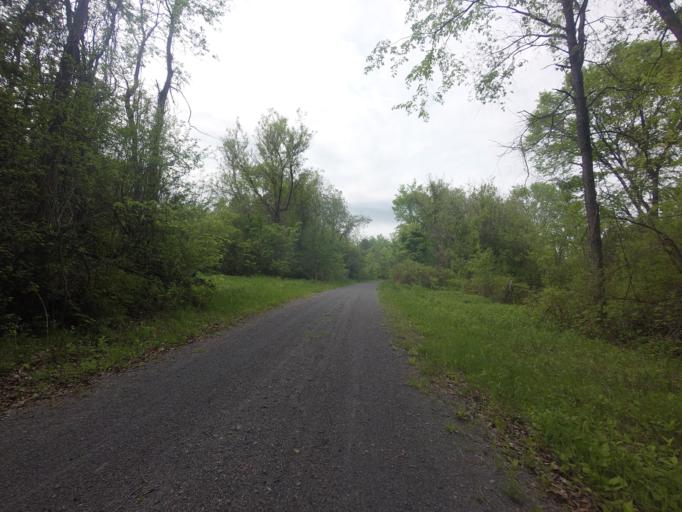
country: CA
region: Ontario
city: Kingston
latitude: 44.3883
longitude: -76.6427
